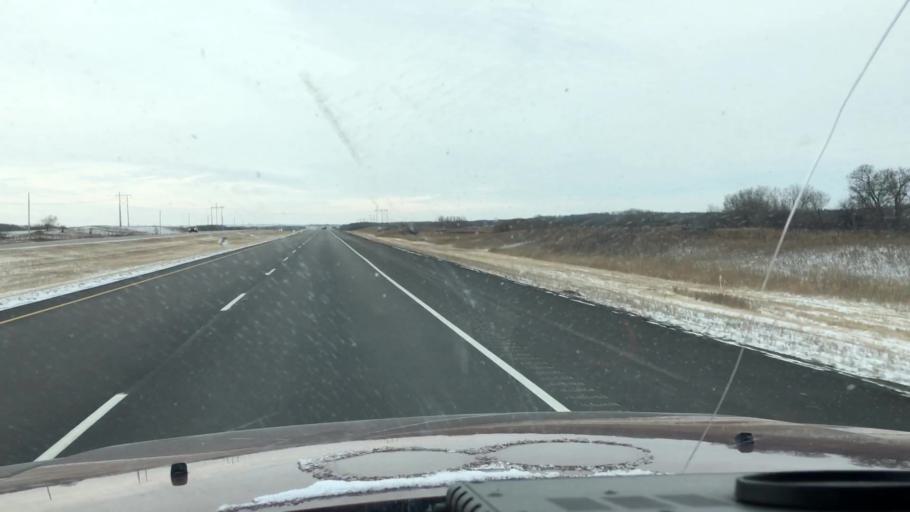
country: CA
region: Saskatchewan
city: Saskatoon
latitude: 51.8969
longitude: -106.5199
